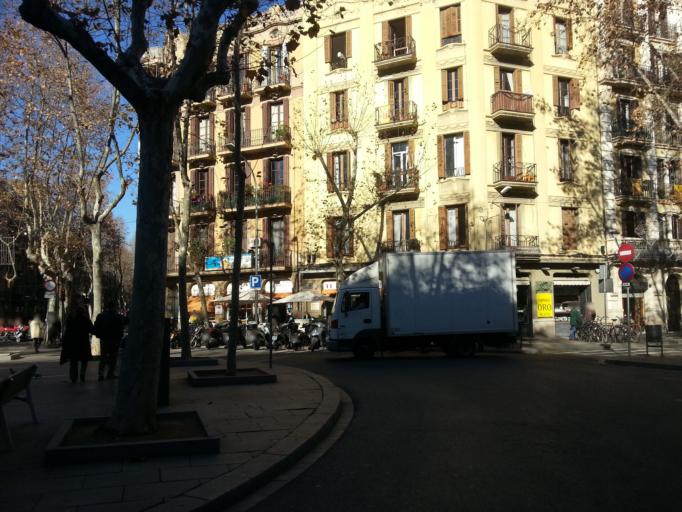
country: ES
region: Catalonia
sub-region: Provincia de Barcelona
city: Sant Marti
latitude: 41.3998
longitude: 2.2031
